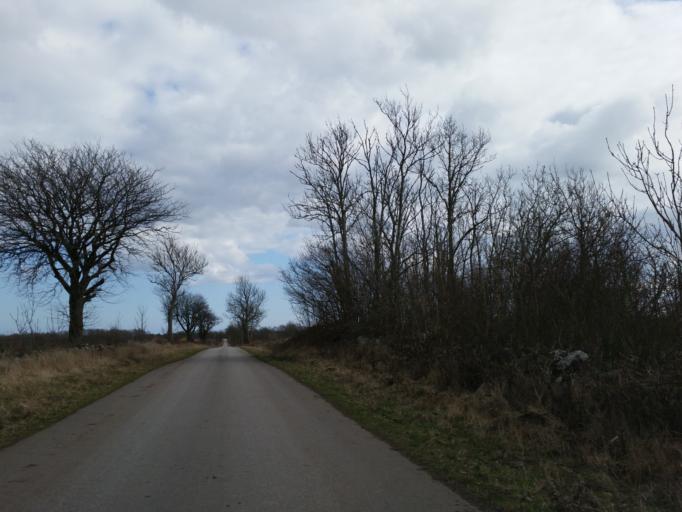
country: SE
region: Kalmar
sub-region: Morbylanga Kommun
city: Sodra Sandby
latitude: 56.6723
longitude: 16.6652
